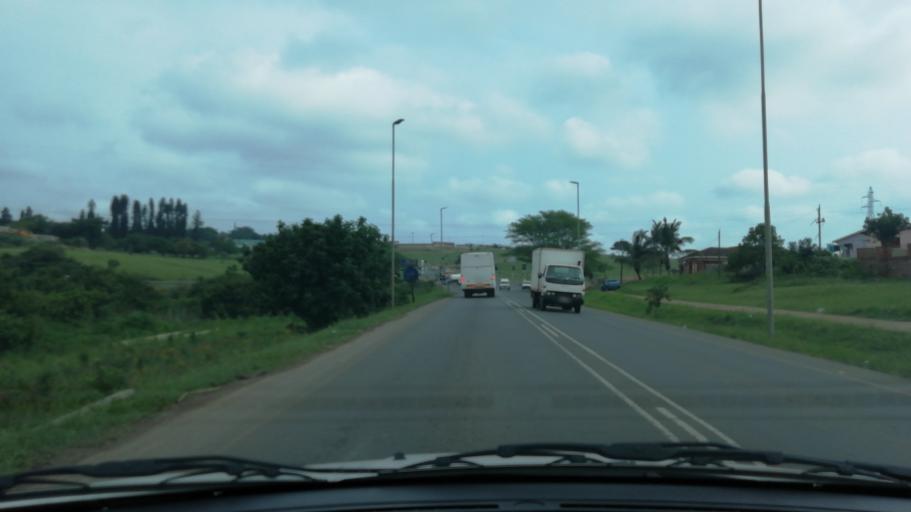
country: ZA
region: KwaZulu-Natal
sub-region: uThungulu District Municipality
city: Empangeni
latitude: -28.7400
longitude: 31.8818
